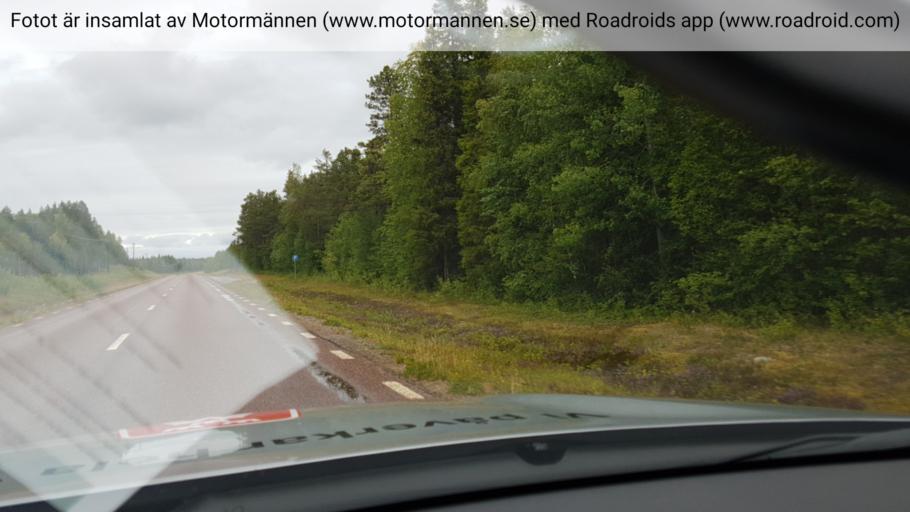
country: SE
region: Norrbotten
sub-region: Pajala Kommun
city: Pajala
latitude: 67.1243
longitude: 22.6061
